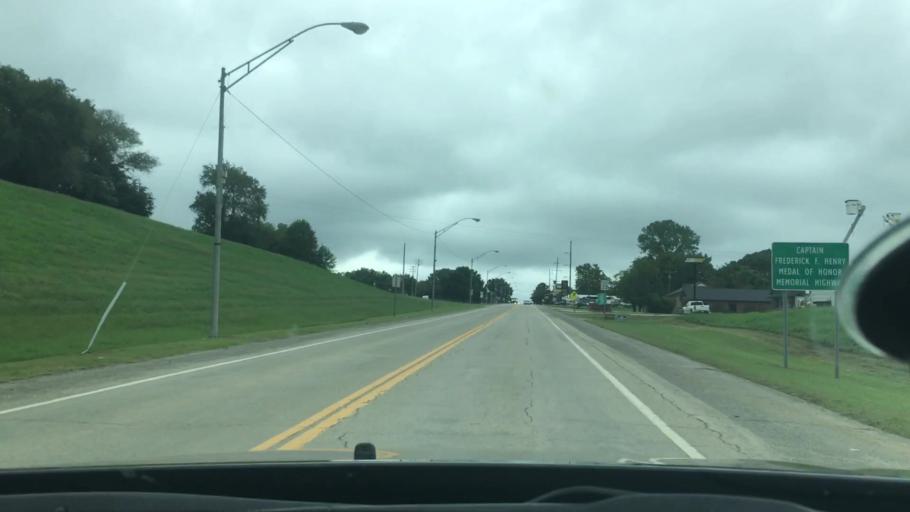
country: US
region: Oklahoma
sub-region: Sequoyah County
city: Vian
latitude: 35.4903
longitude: -94.9723
